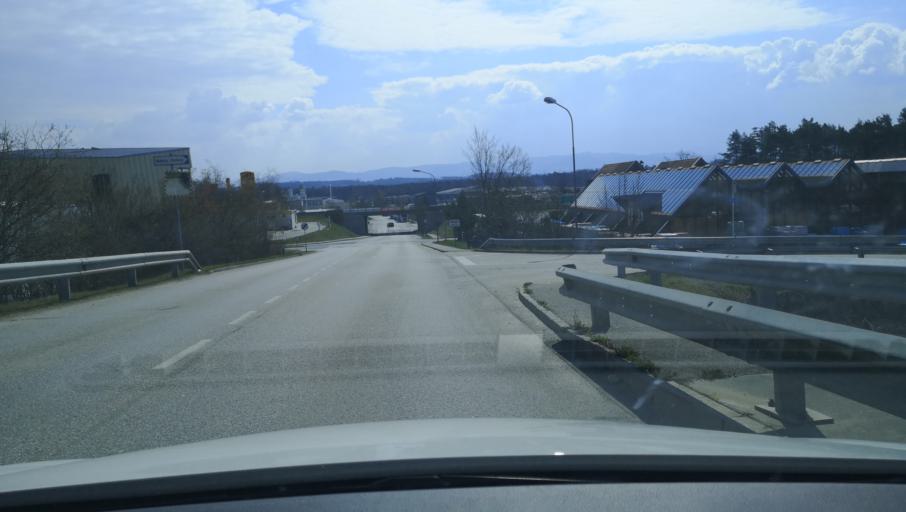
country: AT
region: Lower Austria
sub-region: Politischer Bezirk Amstetten
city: Winklarn
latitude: 48.1029
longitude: 14.8222
